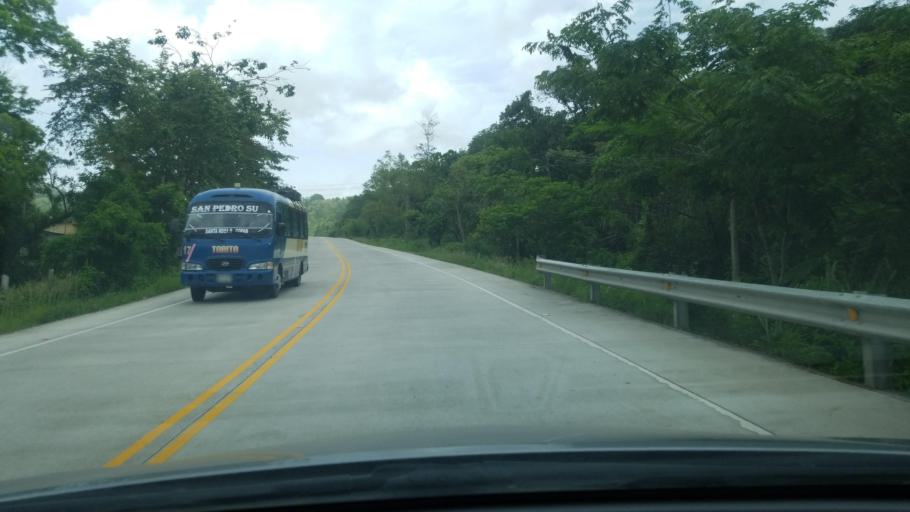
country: HN
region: Copan
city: San Juan de Planes
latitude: 14.9266
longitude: -88.7656
